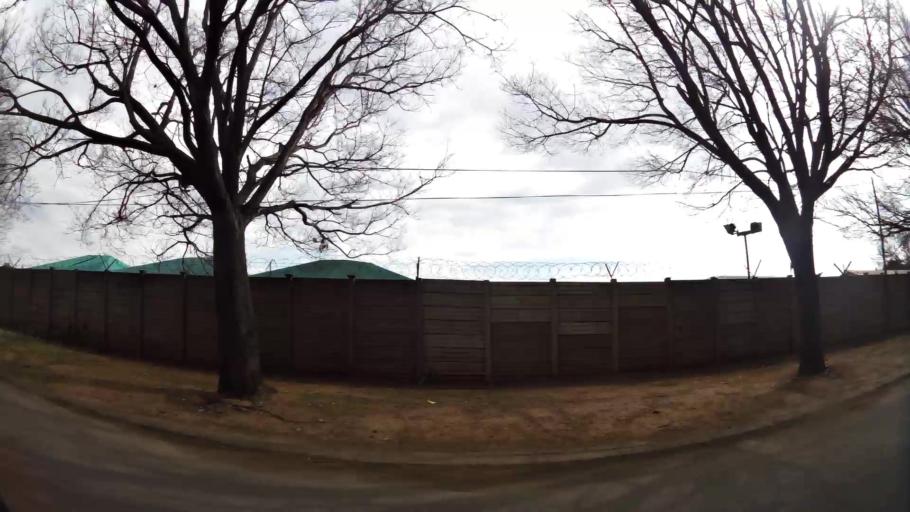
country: ZA
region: Gauteng
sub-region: Sedibeng District Municipality
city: Vanderbijlpark
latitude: -26.6885
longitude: 27.8096
